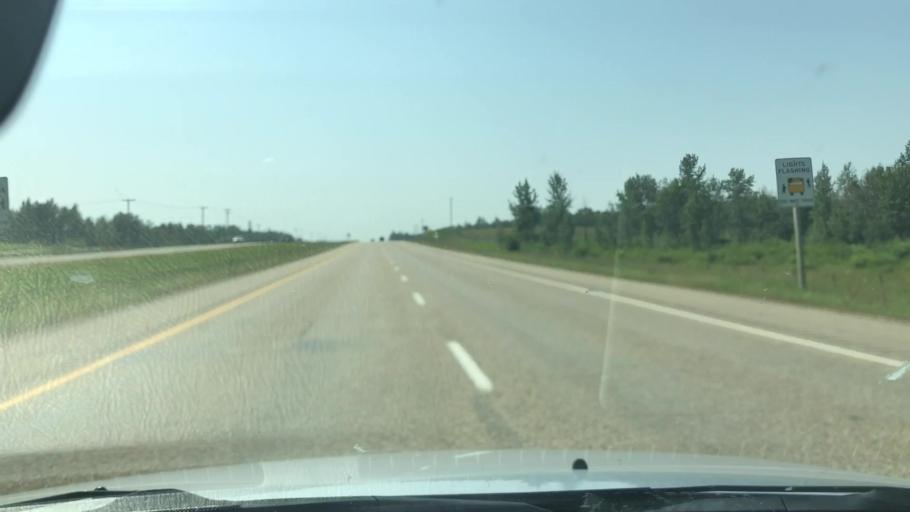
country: CA
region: Alberta
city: Devon
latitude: 53.4429
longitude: -113.7623
